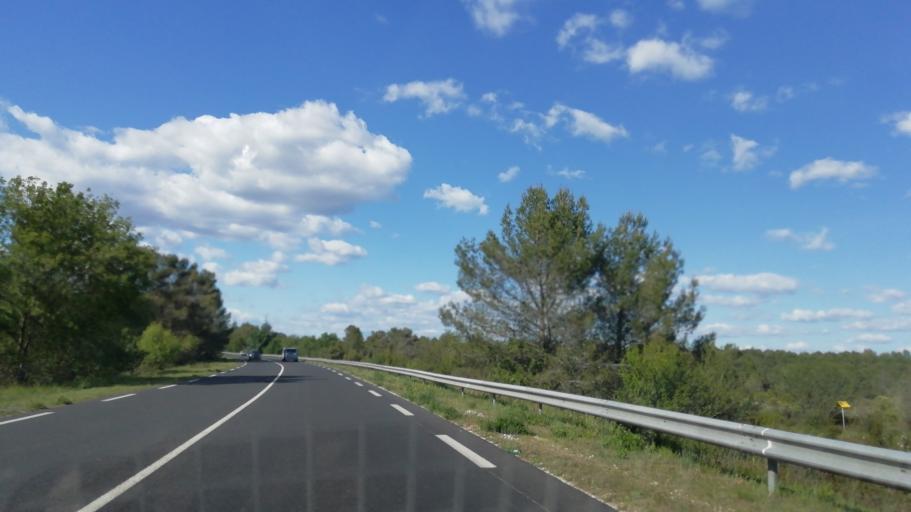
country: FR
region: Languedoc-Roussillon
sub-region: Departement de l'Herault
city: Saint-Clement-de-Riviere
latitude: 43.6930
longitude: 3.8262
